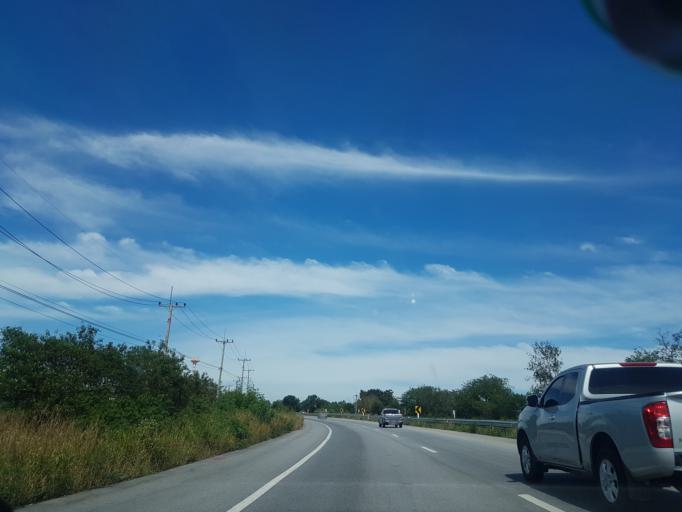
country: TH
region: Rayong
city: Ban Chang
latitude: 12.8609
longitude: 101.0234
